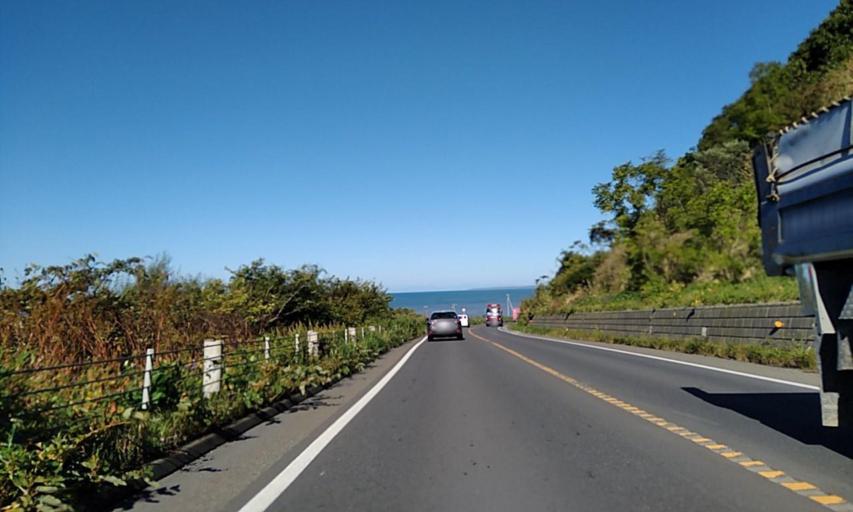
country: JP
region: Hokkaido
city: Shizunai-furukawacho
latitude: 42.3841
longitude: 142.2741
